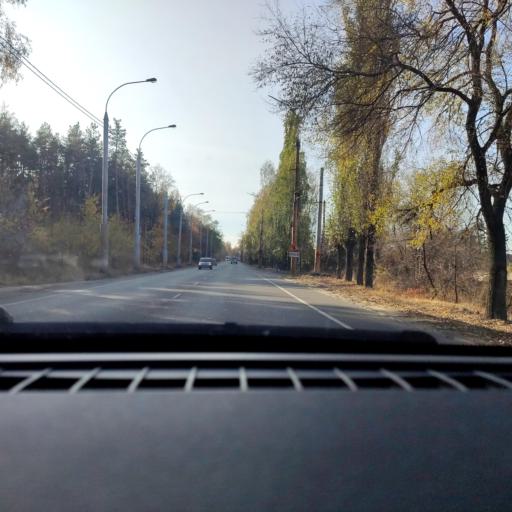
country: RU
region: Voronezj
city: Somovo
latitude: 51.7083
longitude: 39.2917
